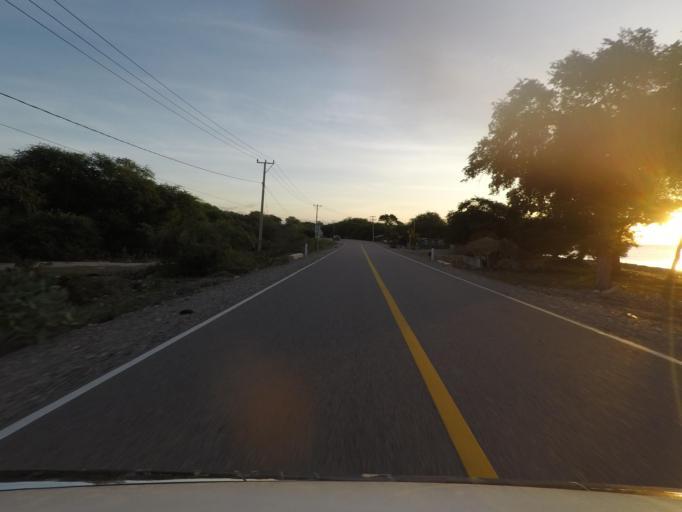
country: TL
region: Baucau
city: Baucau
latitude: -8.4250
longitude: 126.6973
